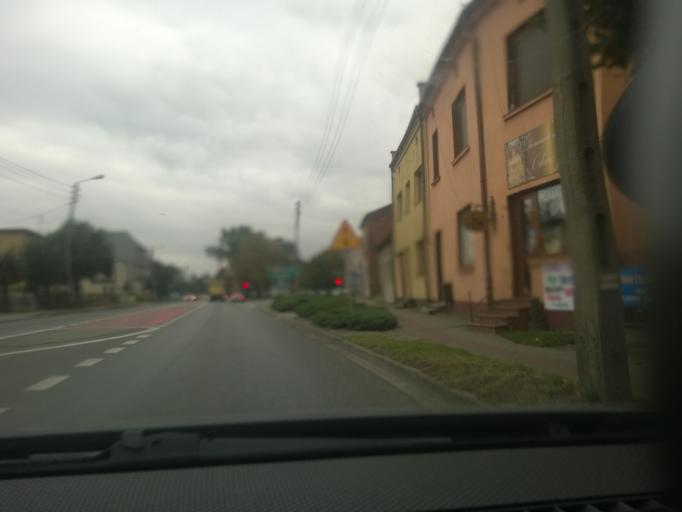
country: PL
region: Greater Poland Voivodeship
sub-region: Powiat kaliski
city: Opatowek
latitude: 51.7393
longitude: 18.2128
